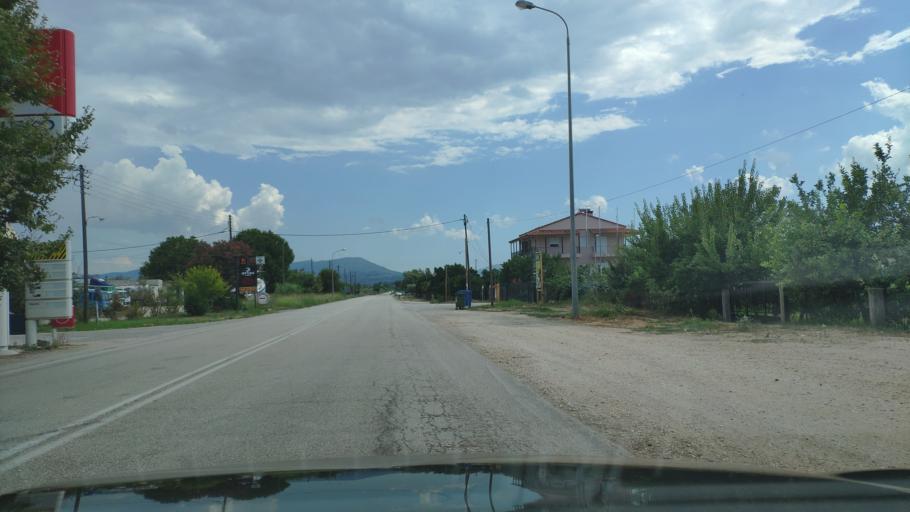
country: GR
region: West Greece
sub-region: Nomos Aitolias kai Akarnanias
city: Krikellos
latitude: 38.9460
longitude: 21.1764
